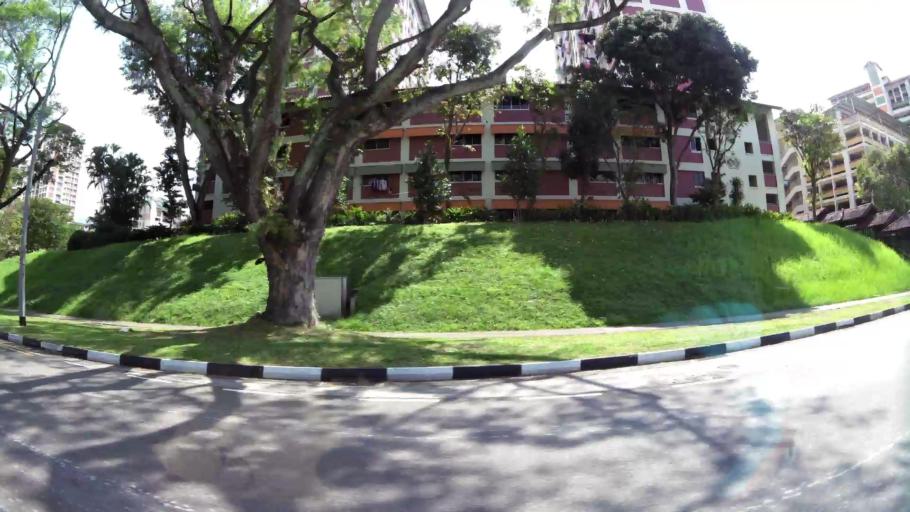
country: SG
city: Singapore
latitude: 1.3599
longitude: 103.8416
